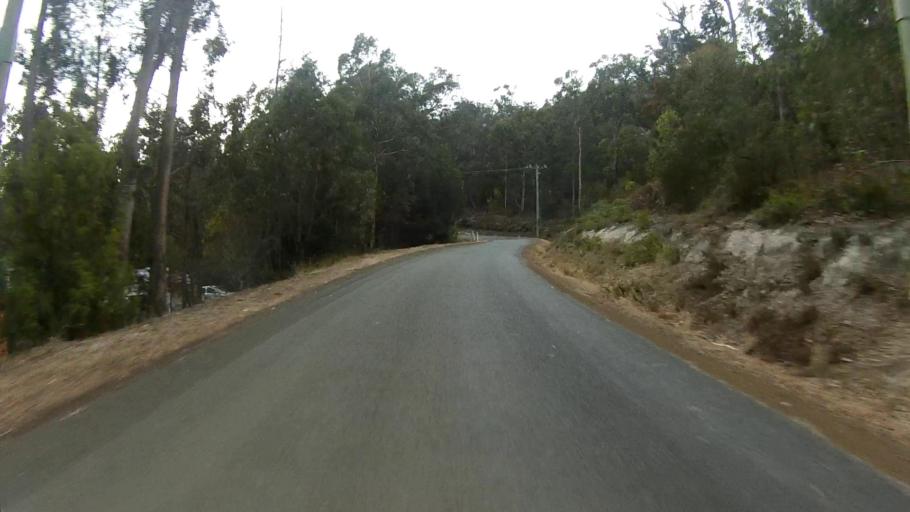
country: AU
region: Tasmania
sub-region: Huon Valley
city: Cygnet
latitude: -43.2173
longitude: 147.0961
